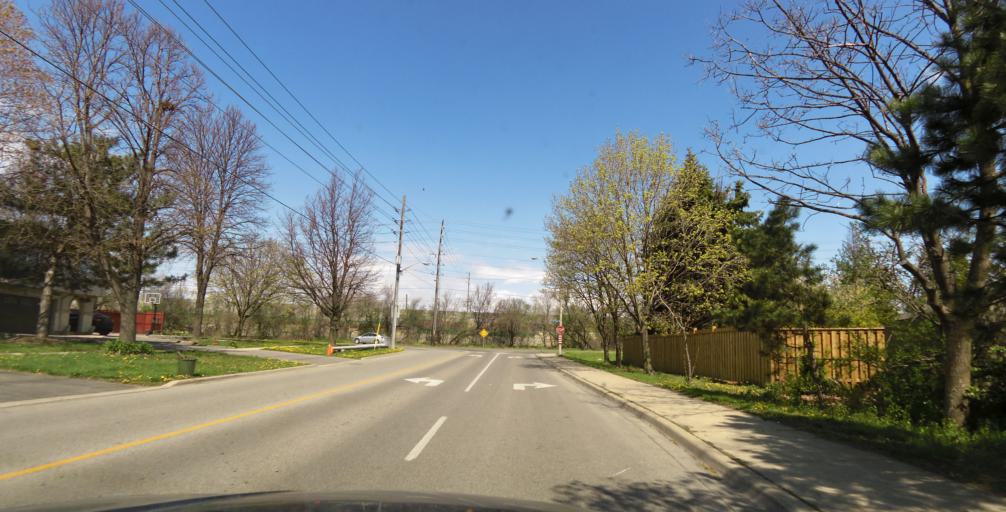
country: CA
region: Ontario
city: Mississauga
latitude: 43.5296
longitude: -79.6406
